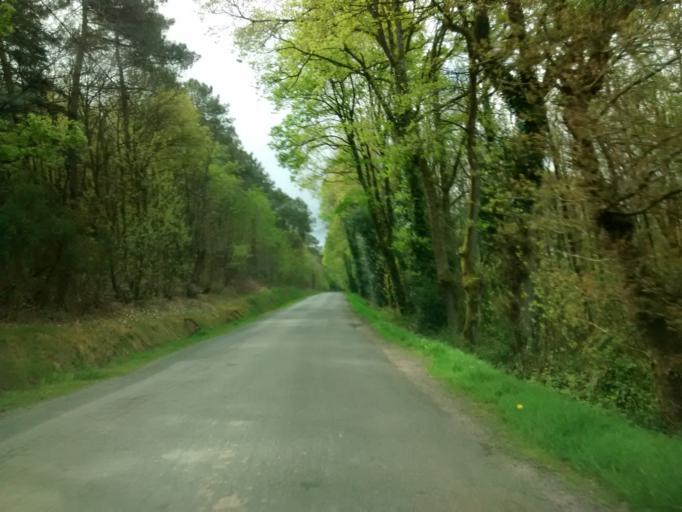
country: FR
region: Brittany
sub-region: Departement du Morbihan
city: Ruffiac
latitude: 47.7764
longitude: -2.3135
